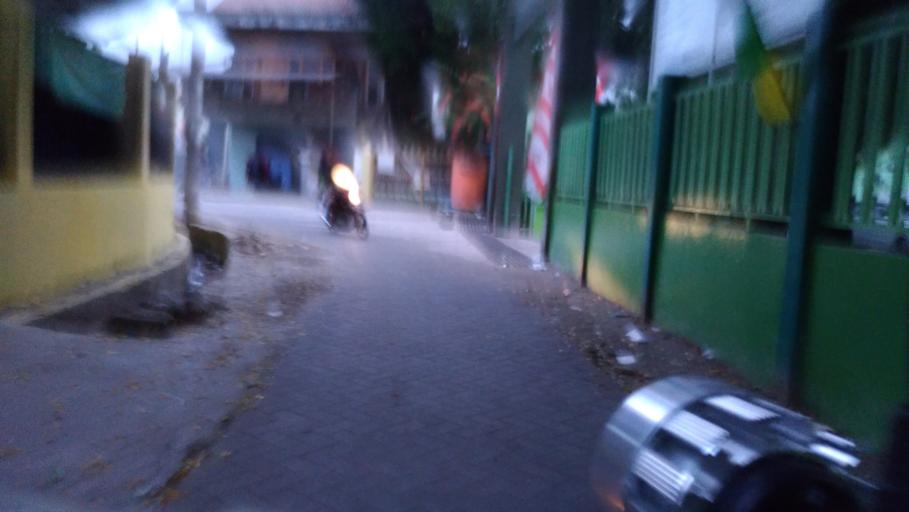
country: ID
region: West Java
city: Depok
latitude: -6.3510
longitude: 106.8700
